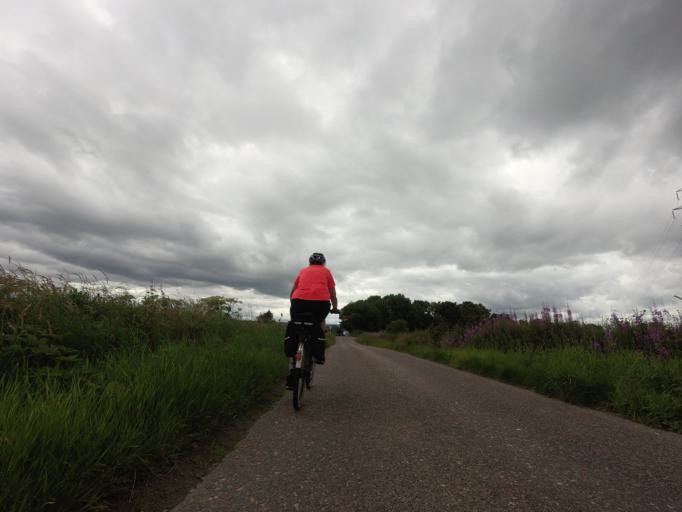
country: GB
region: Scotland
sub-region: Moray
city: Forres
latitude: 57.6116
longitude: -3.6857
